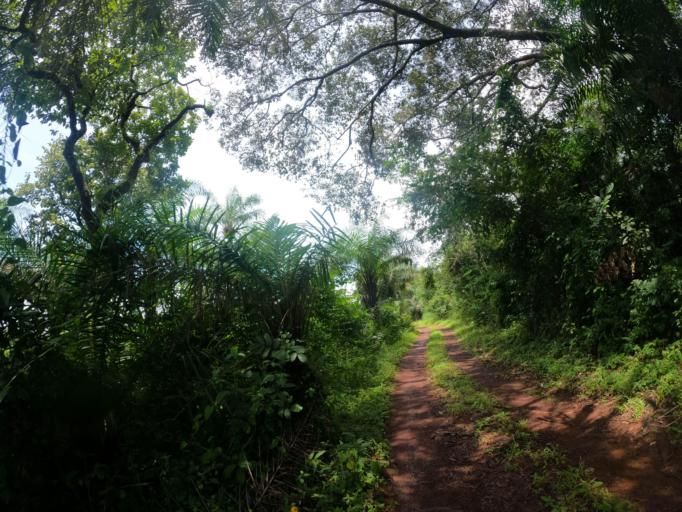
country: SL
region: Northern Province
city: Binkolo
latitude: 9.1545
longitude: -12.1955
